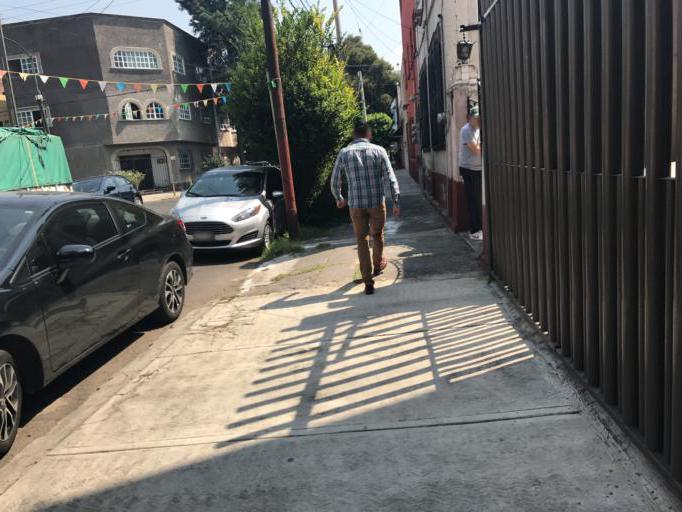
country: MX
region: Mexico
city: Colonia Lindavista
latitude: 19.4730
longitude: -99.1249
